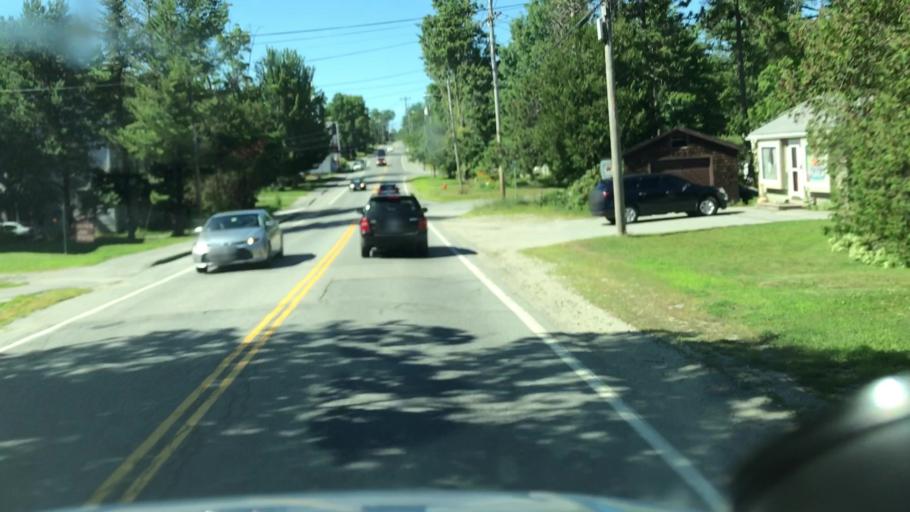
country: US
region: Maine
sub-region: Hancock County
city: Ellsworth
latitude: 44.5443
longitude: -68.4253
